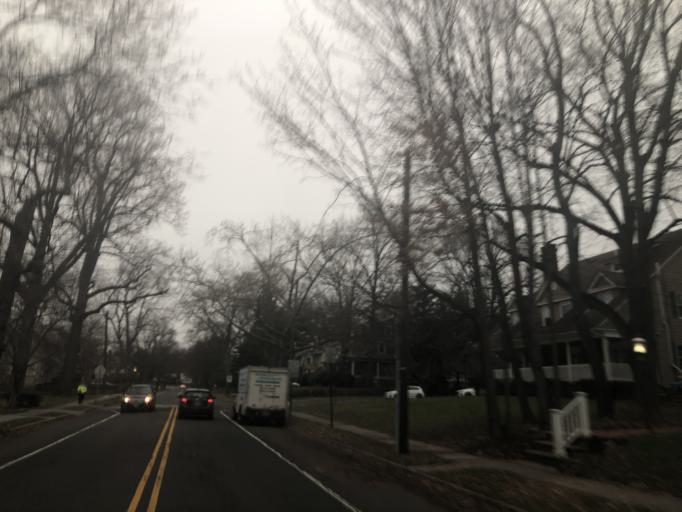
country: US
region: New Jersey
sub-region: Essex County
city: Maplewood
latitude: 40.7361
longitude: -74.2618
